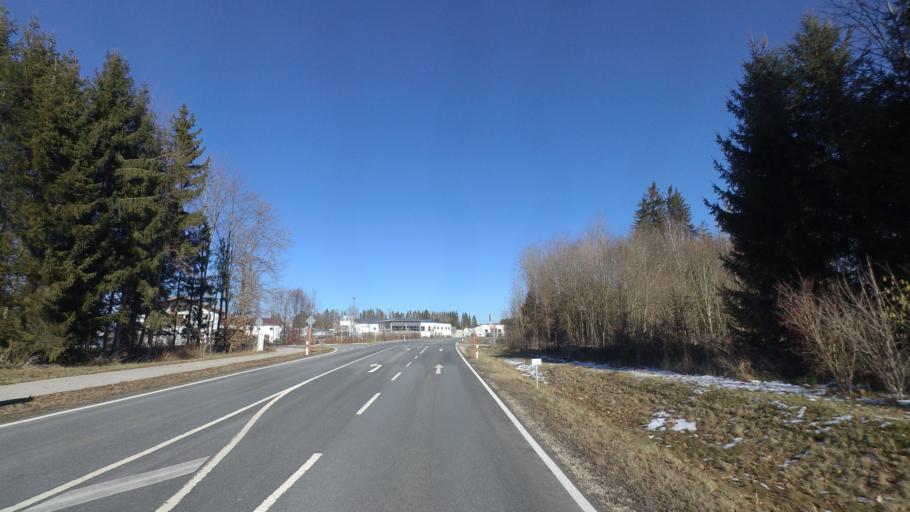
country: DE
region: Bavaria
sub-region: Upper Bavaria
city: Traunreut
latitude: 47.9478
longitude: 12.6077
